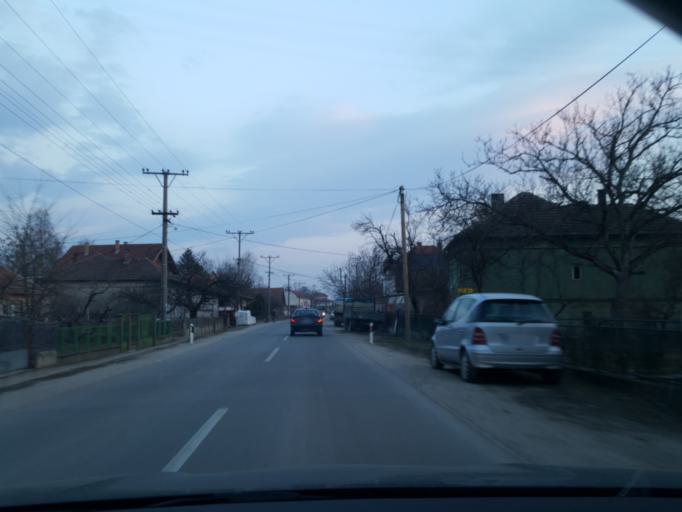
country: RS
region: Central Serbia
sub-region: Nisavski Okrug
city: Aleksinac
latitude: 43.5028
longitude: 21.7006
